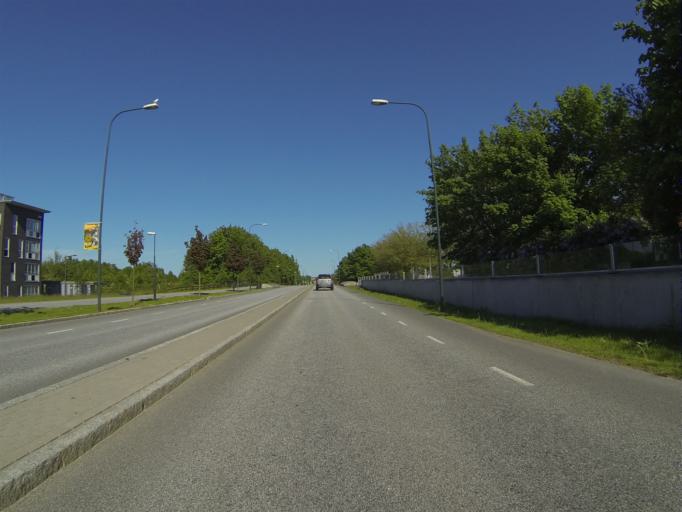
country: SE
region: Skane
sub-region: Burlovs Kommun
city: Arloev
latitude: 55.5948
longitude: 13.0686
